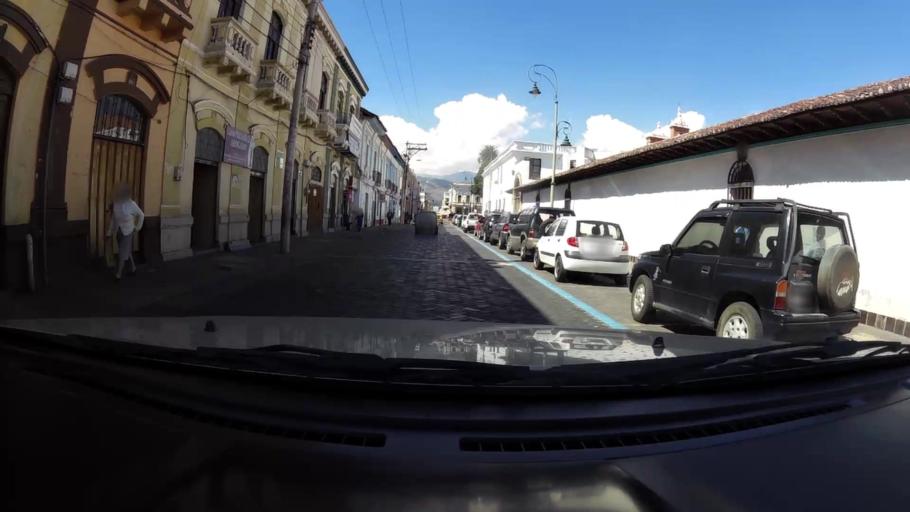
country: EC
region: Chimborazo
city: Riobamba
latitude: -1.6722
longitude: -78.6474
